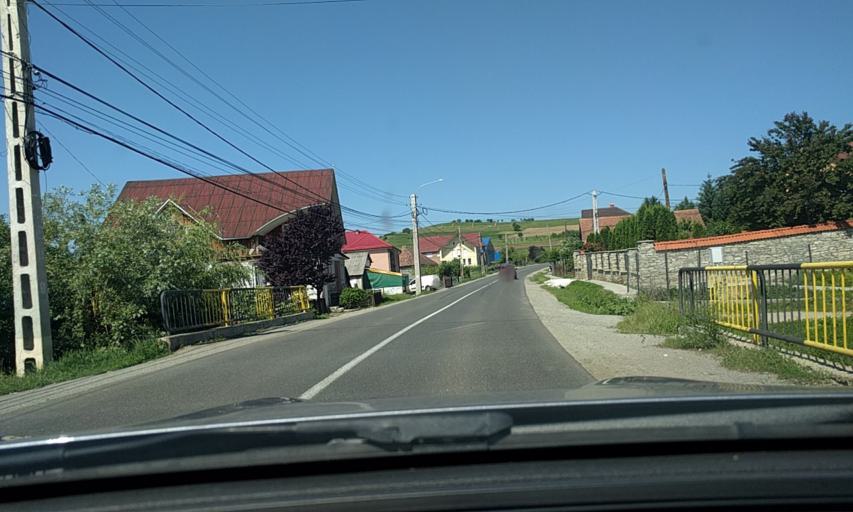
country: RO
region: Bistrita-Nasaud
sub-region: Comuna Dumitra
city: Dumitra
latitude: 47.2241
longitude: 24.4610
